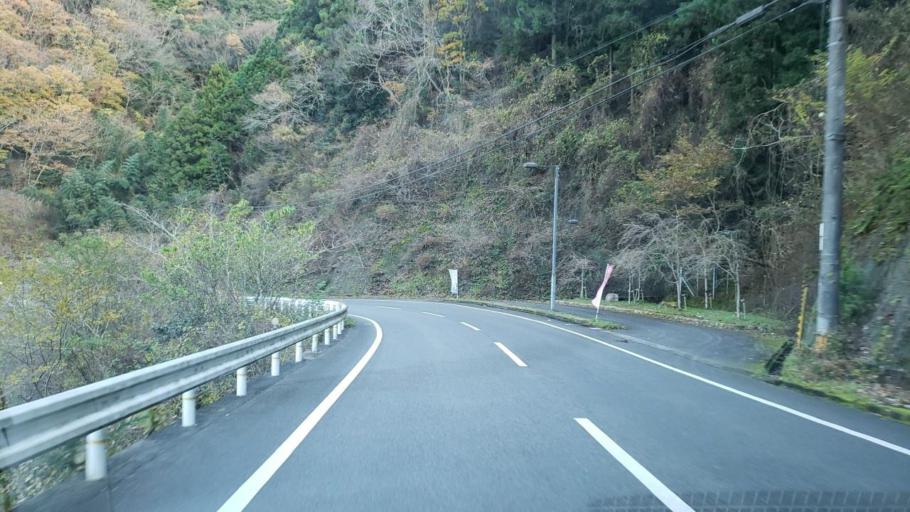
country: JP
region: Tokushima
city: Wakimachi
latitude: 34.1676
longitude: 134.0754
